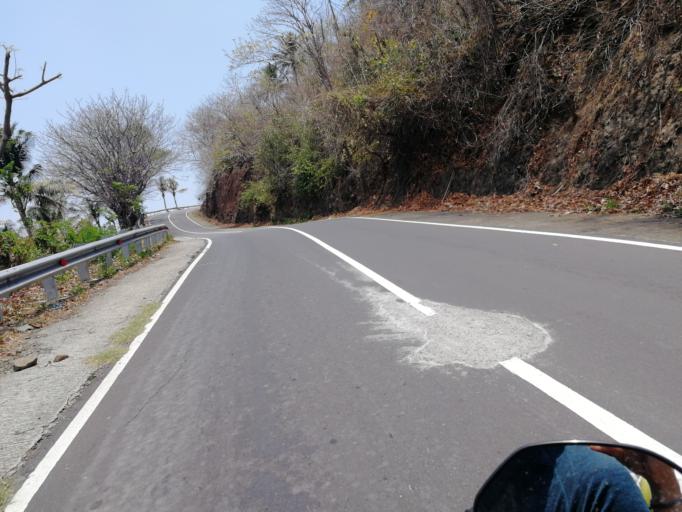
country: ID
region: West Nusa Tenggara
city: Karangsubagan
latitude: -8.4491
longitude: 116.0352
